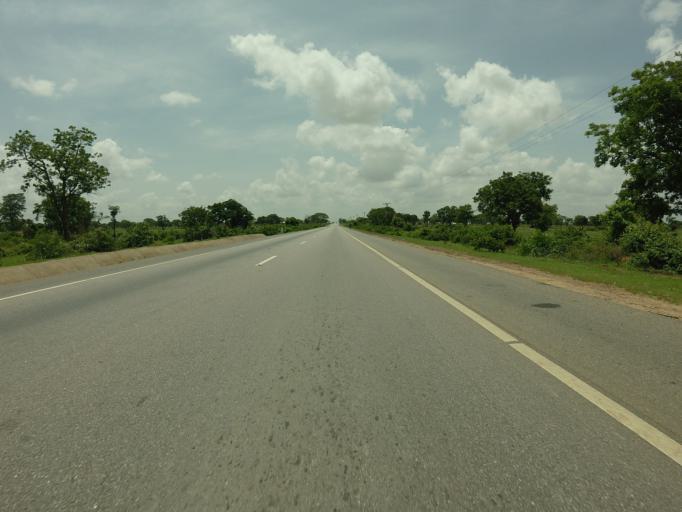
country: GH
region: Northern
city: Tamale
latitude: 9.2987
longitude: -0.9654
